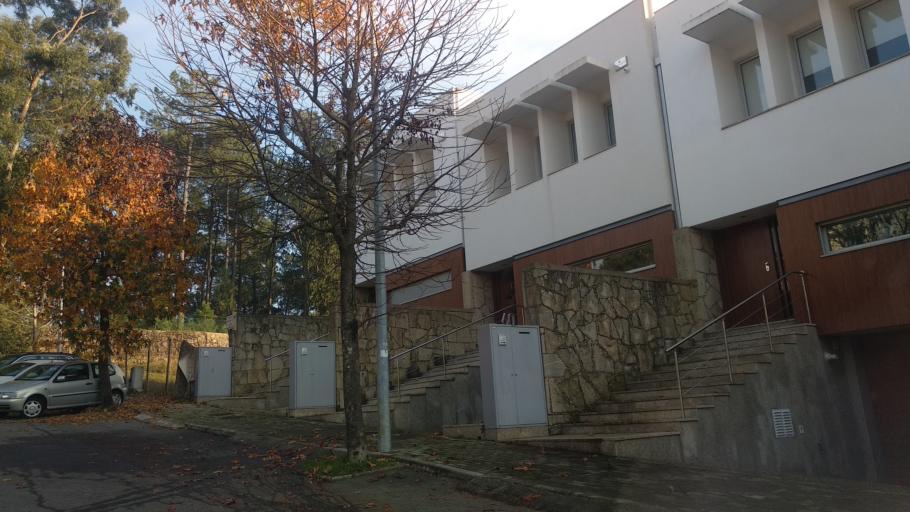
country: PT
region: Braga
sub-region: Braga
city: Adaufe
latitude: 41.5730
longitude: -8.3767
